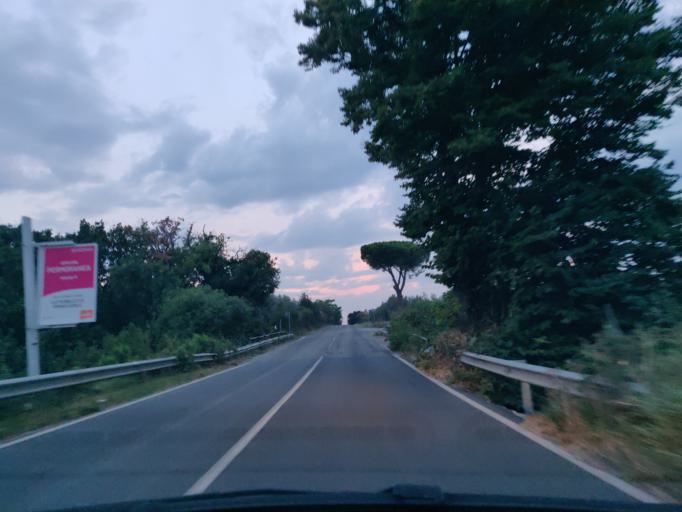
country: IT
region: Latium
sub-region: Provincia di Viterbo
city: San Martino al Cimino
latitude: 42.3789
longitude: 12.0714
